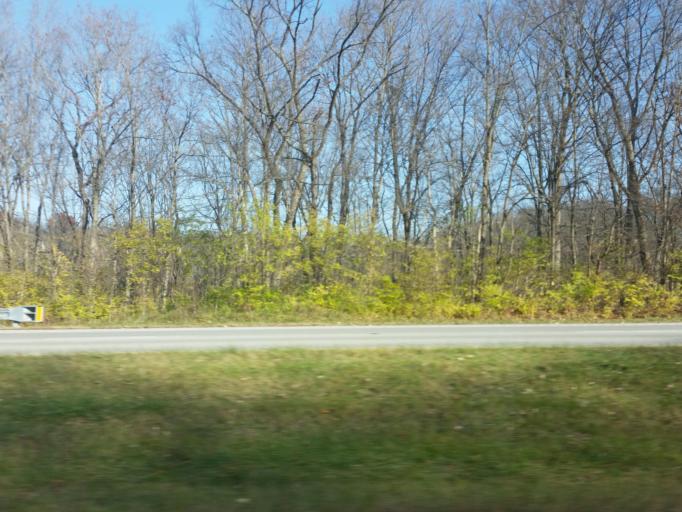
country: US
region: Ohio
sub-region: Hamilton County
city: Dunlap
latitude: 39.3013
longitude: -84.6212
